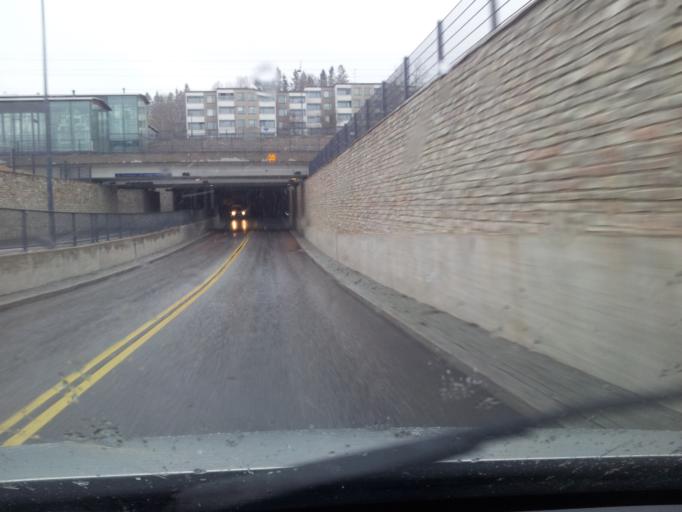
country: FI
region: Uusimaa
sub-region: Helsinki
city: Espoo
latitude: 60.1911
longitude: 24.6068
